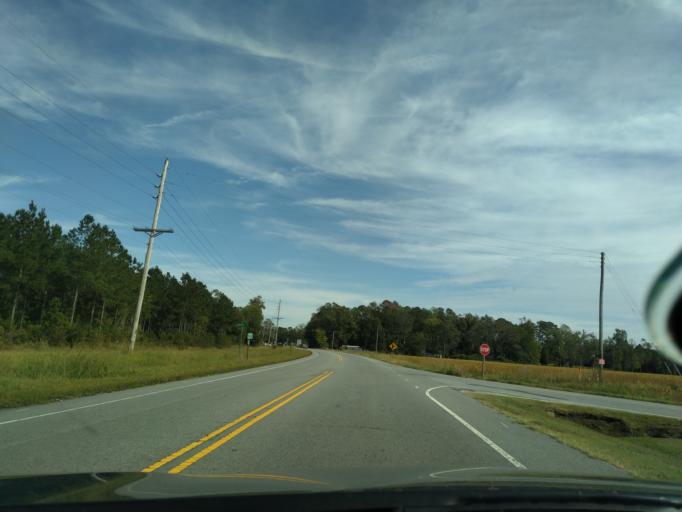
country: US
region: North Carolina
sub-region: Beaufort County
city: River Road
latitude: 35.5125
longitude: -76.9090
